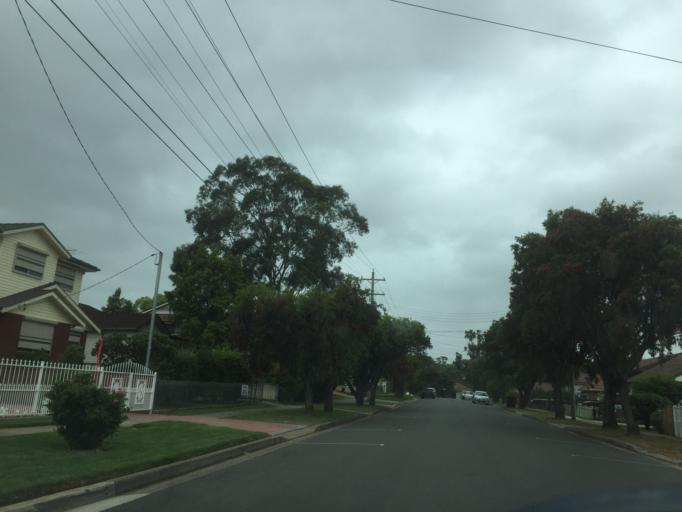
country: AU
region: New South Wales
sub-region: Blacktown
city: Blacktown
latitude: -33.7750
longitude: 150.8994
